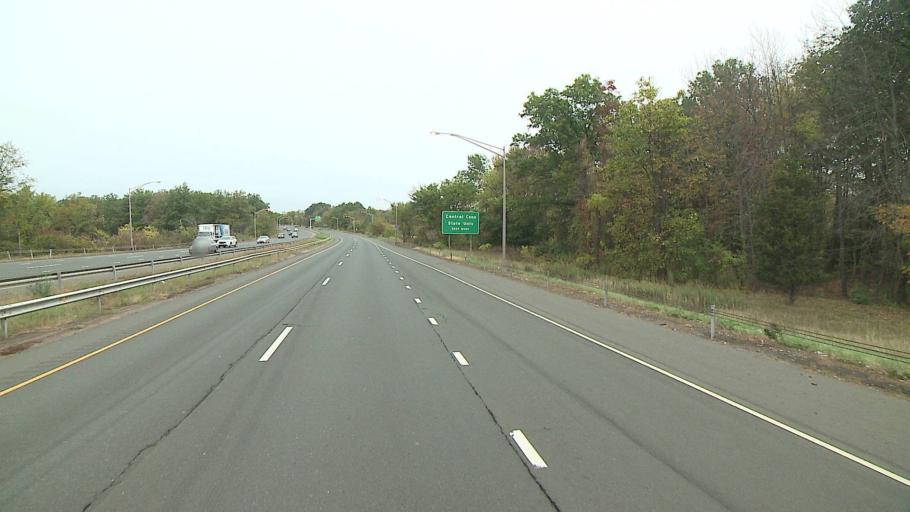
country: US
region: Connecticut
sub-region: Hartford County
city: Kensington
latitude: 41.6387
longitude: -72.7538
